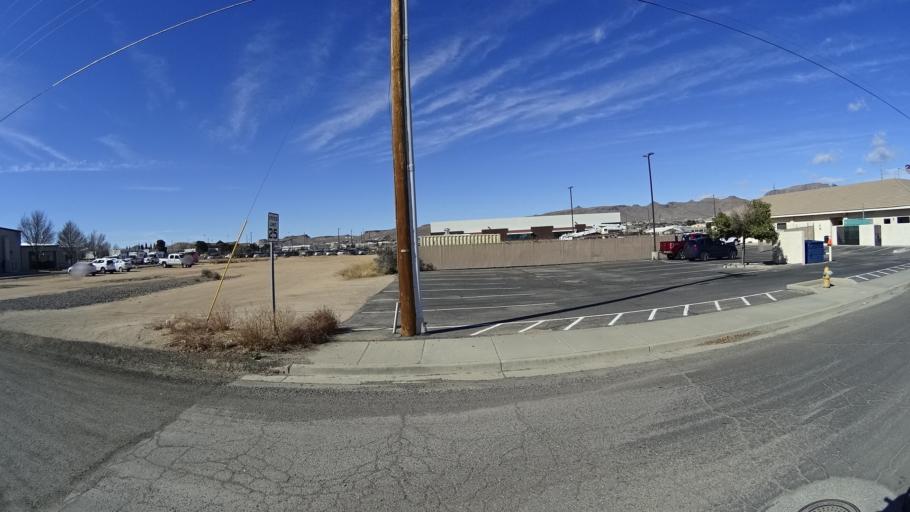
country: US
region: Arizona
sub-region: Mohave County
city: New Kingman-Butler
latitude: 35.2238
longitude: -114.0203
